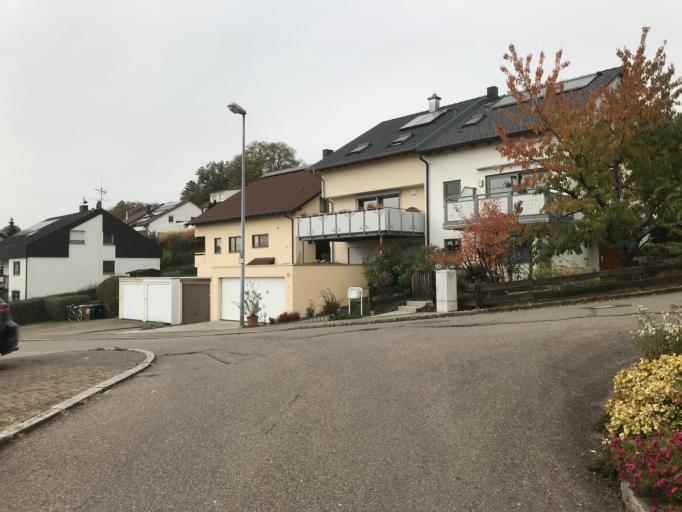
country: DE
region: Baden-Wuerttemberg
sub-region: Regierungsbezirk Stuttgart
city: Unterensingen
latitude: 48.6477
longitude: 9.3490
